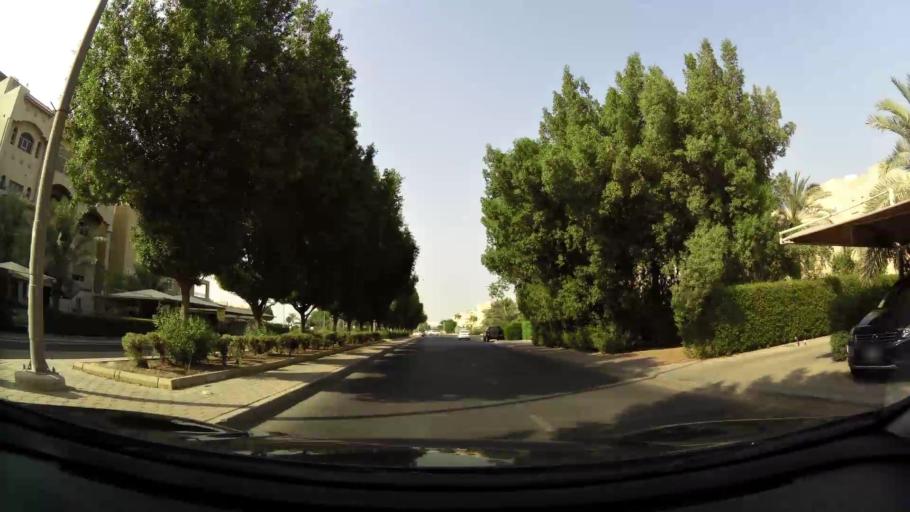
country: KW
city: Bayan
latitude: 29.2823
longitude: 48.0461
